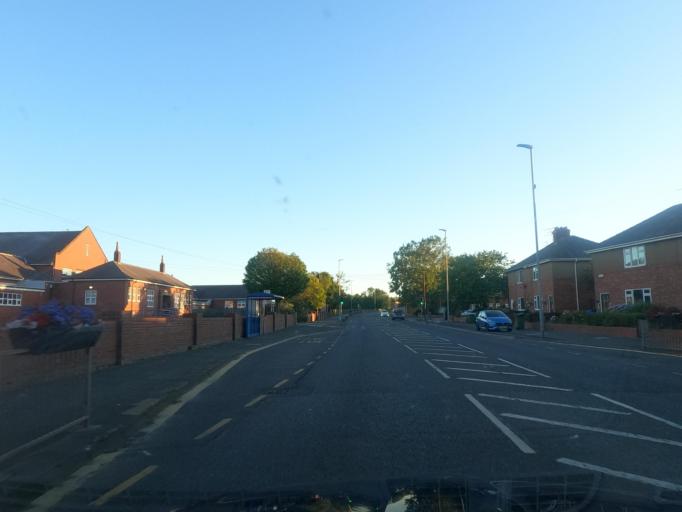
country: GB
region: England
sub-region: Northumberland
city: Bedlington
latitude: 55.1294
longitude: -1.5509
